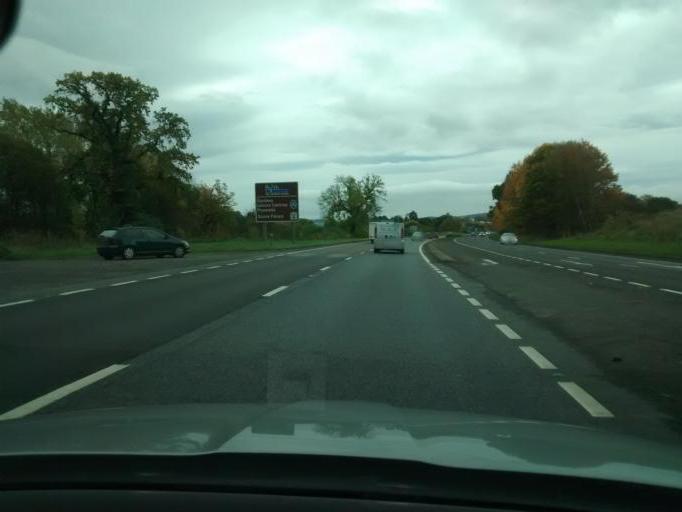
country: GB
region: Scotland
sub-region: Perth and Kinross
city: Luncarty
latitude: 56.4282
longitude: -3.4687
